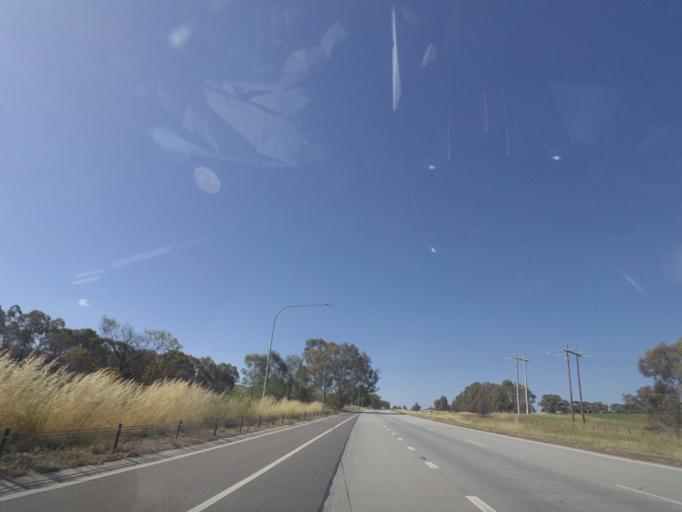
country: AU
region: New South Wales
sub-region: Albury Municipality
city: Lavington
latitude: -35.9965
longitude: 146.9929
